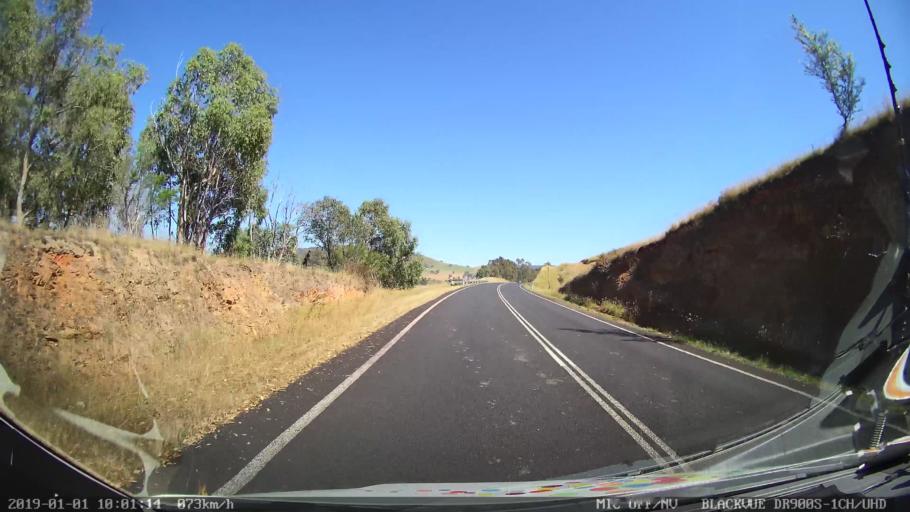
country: AU
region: New South Wales
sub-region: Snowy River
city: Jindabyne
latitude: -36.1937
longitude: 148.1020
